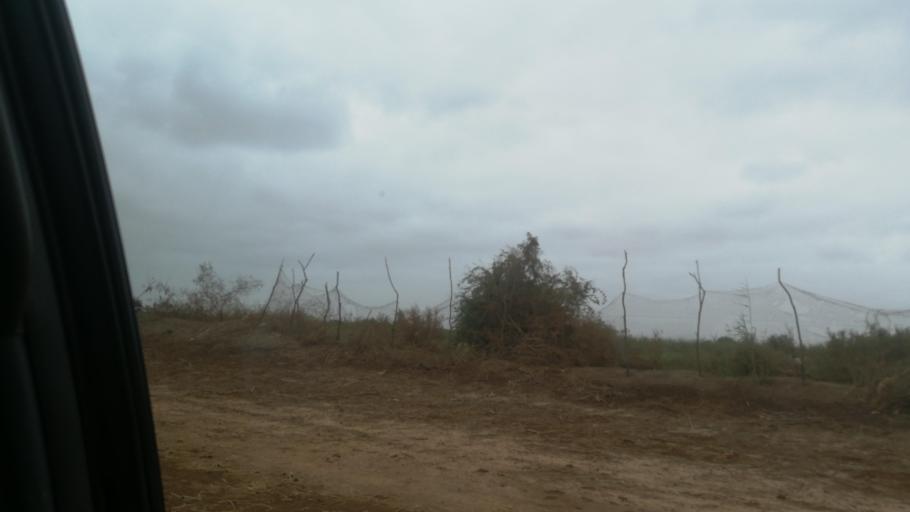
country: SN
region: Saint-Louis
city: Rosso
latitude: 16.2799
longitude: -16.1618
